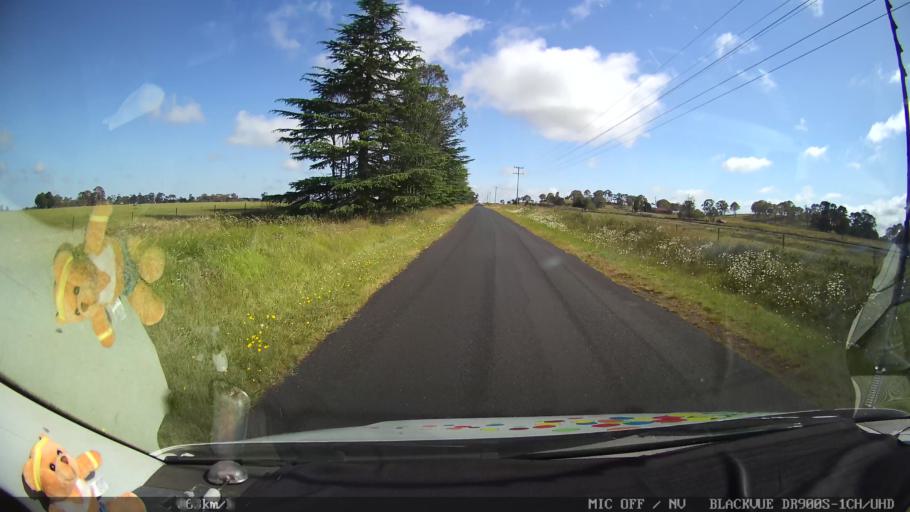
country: AU
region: New South Wales
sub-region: Guyra
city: Guyra
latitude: -30.2023
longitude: 151.6747
